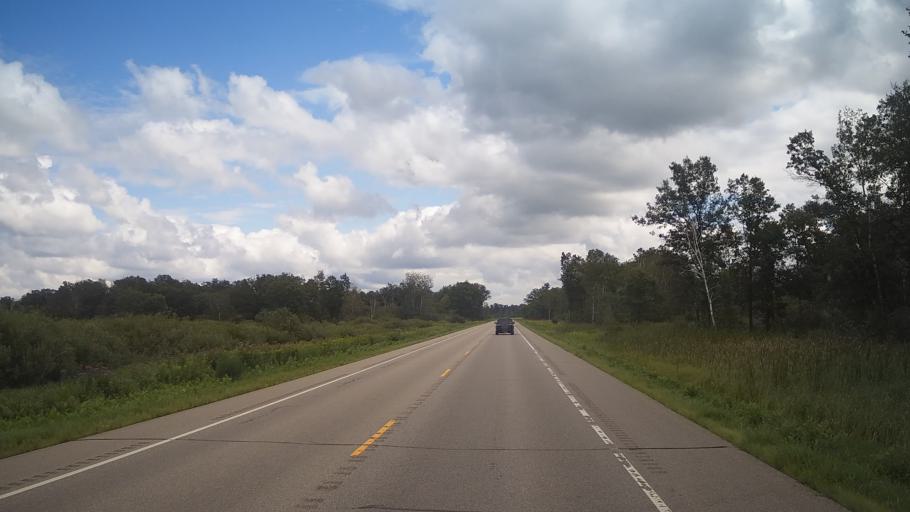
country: US
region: Wisconsin
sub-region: Adams County
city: Friendship
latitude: 44.0257
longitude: -89.6969
